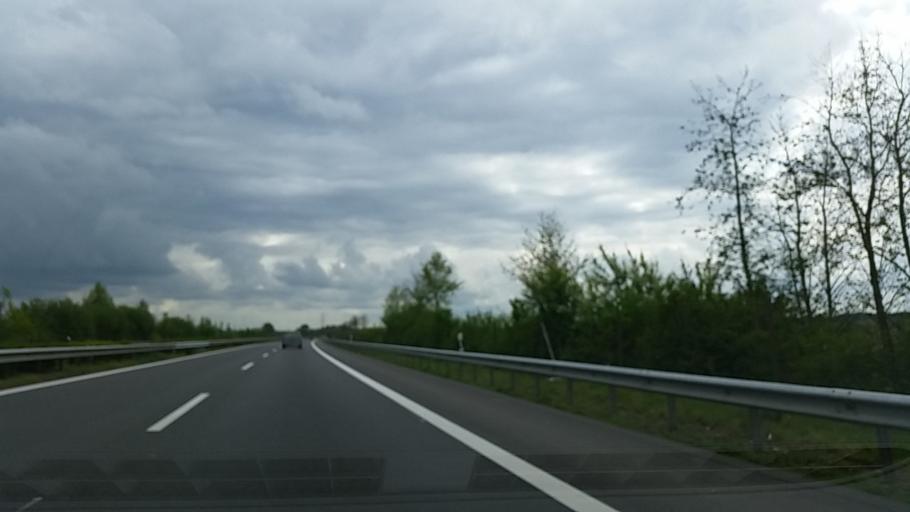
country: DE
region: Lower Saxony
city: Horneburg
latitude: 53.5335
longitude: 9.5784
